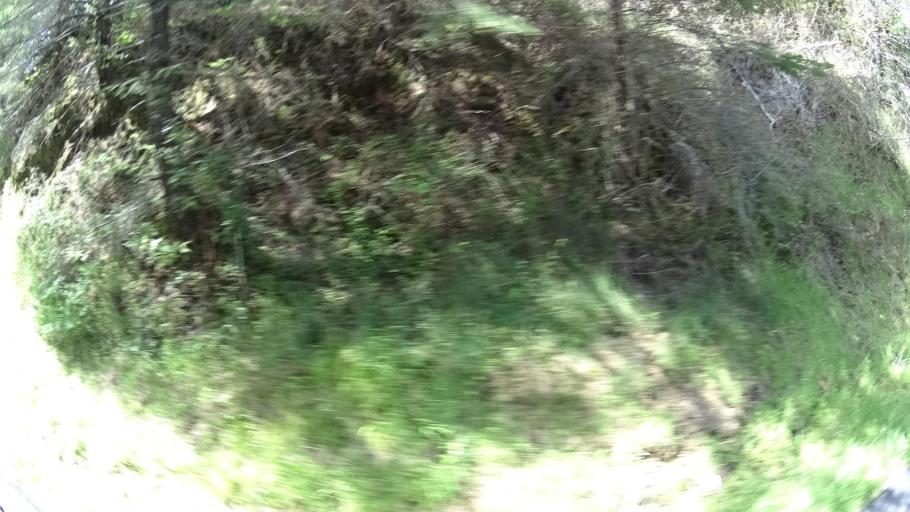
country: US
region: California
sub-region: Humboldt County
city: Redway
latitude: 40.4350
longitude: -123.7730
